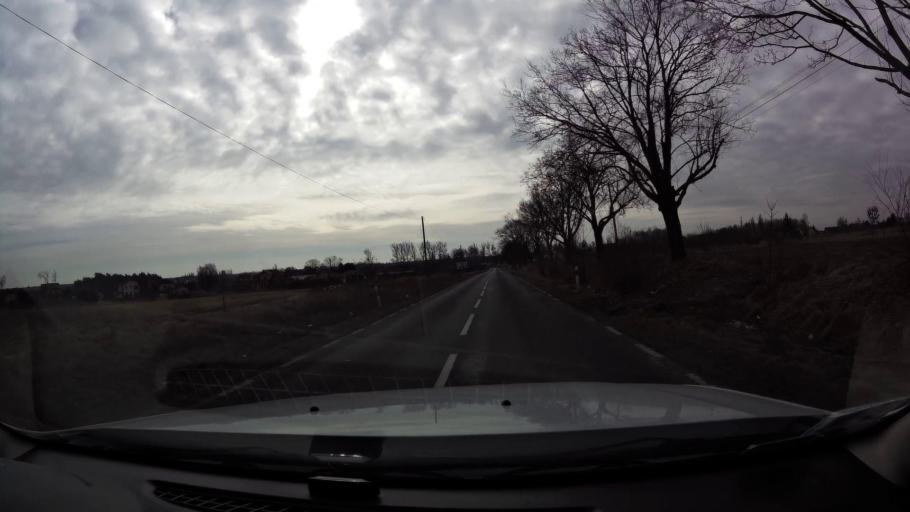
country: PL
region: West Pomeranian Voivodeship
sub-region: Powiat mysliborski
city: Debno
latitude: 52.7498
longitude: 14.6901
